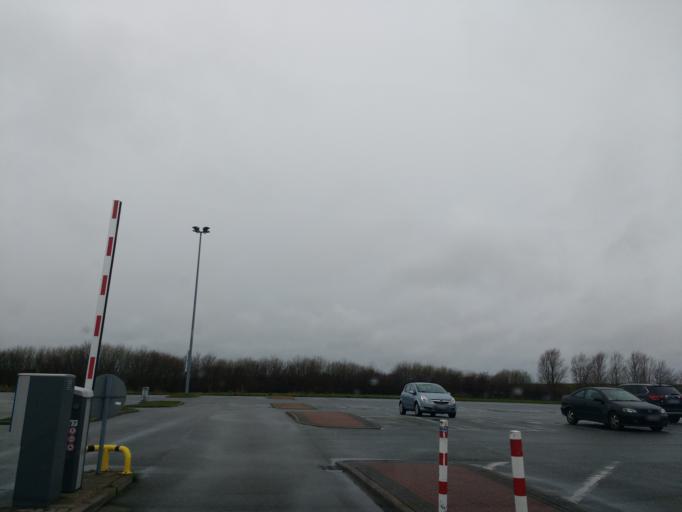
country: DE
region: Schleswig-Holstein
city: Fehmarn
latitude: 54.5026
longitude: 11.2232
